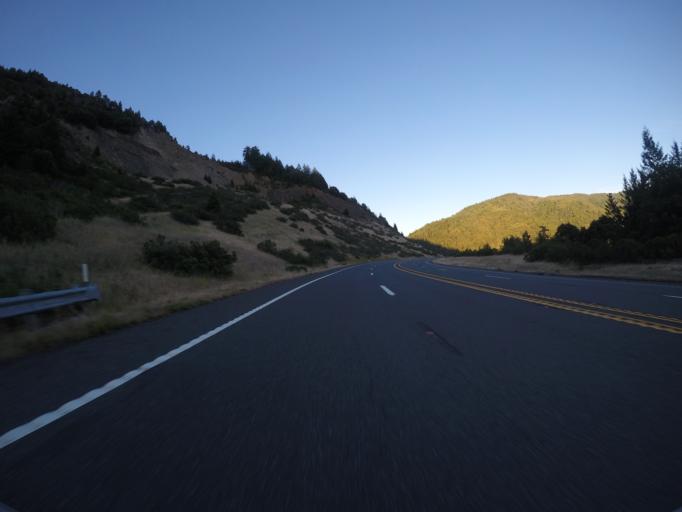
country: US
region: California
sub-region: Mendocino County
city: Laytonville
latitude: 39.8292
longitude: -123.6605
